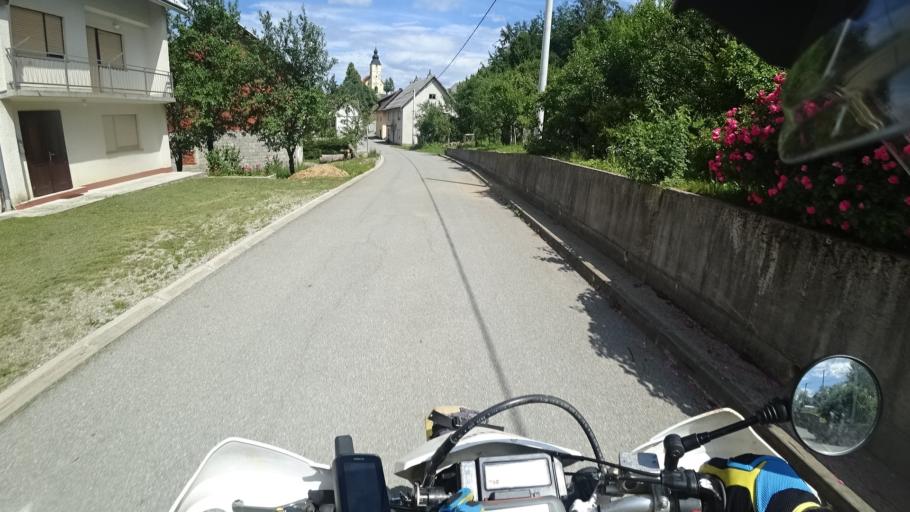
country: SI
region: Osilnica
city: Osilnica
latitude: 45.5143
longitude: 14.6739
